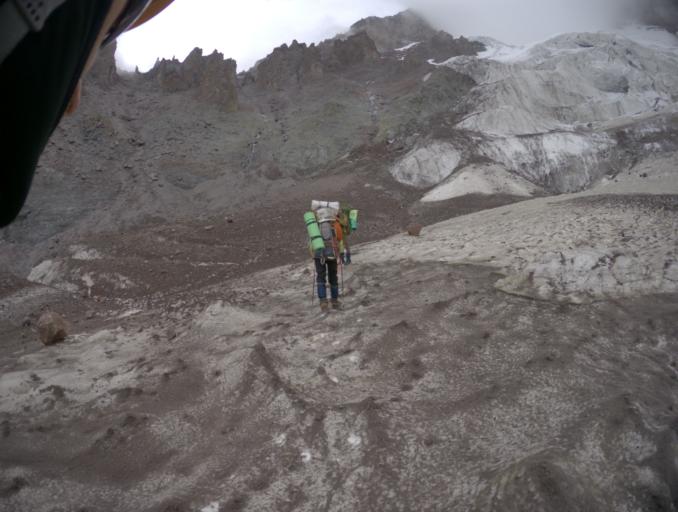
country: RU
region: Kabardino-Balkariya
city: Terskol
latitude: 43.3776
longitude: 42.4023
